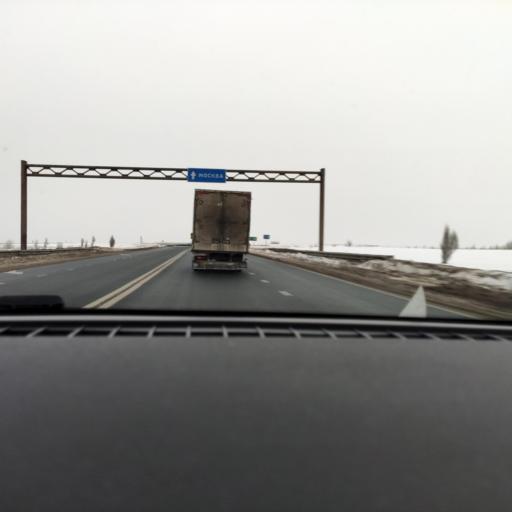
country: RU
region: Samara
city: Petra-Dubrava
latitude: 53.3343
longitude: 50.4531
